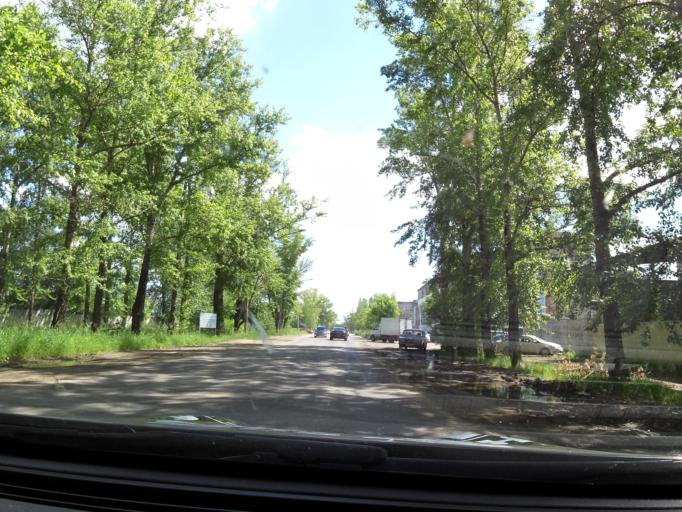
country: RU
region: Vologda
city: Vologda
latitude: 59.2360
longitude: 39.8255
